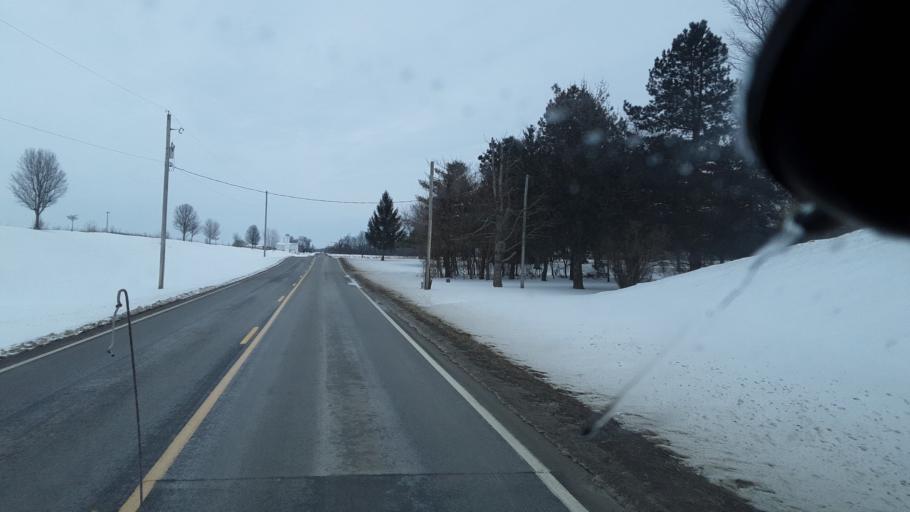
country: US
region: Ohio
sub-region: Union County
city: New California
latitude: 40.2146
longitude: -83.1930
